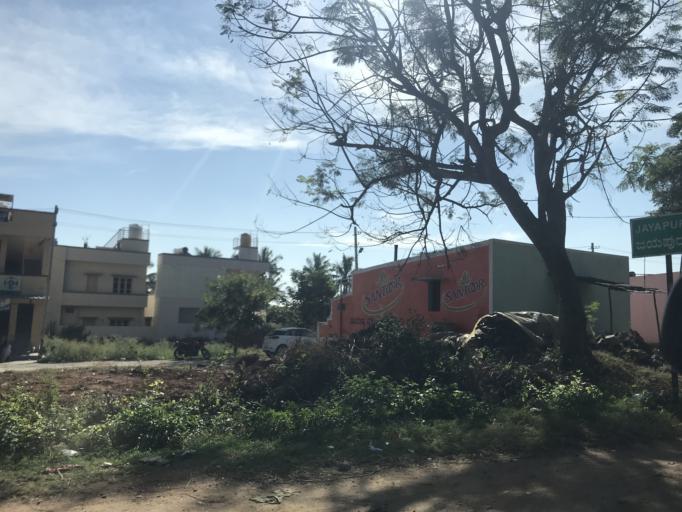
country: IN
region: Karnataka
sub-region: Mysore
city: Mysore
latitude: 12.2052
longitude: 76.5556
